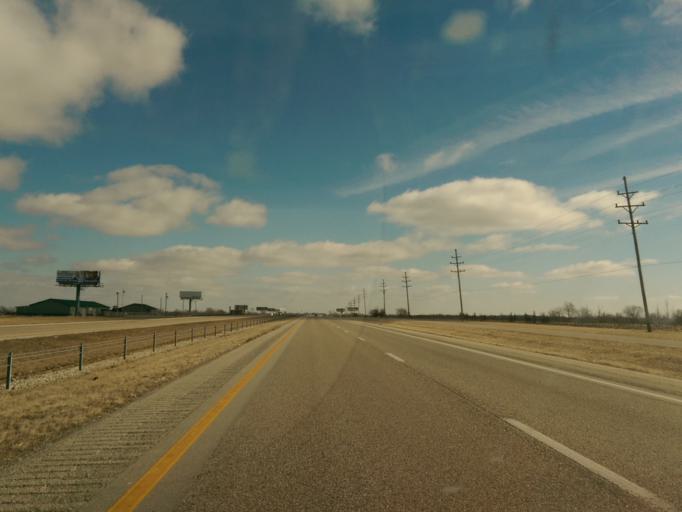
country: US
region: Missouri
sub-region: Montgomery County
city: Montgomery City
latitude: 38.8890
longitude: -91.4191
